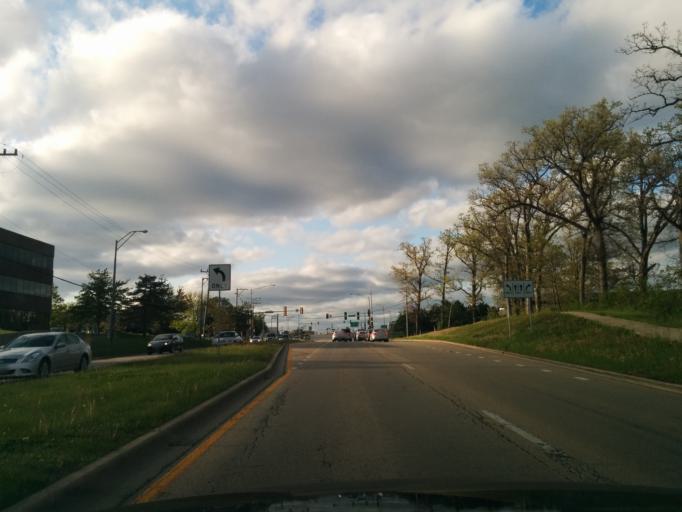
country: US
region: Illinois
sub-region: DuPage County
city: Downers Grove
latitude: 41.8296
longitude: -88.0108
